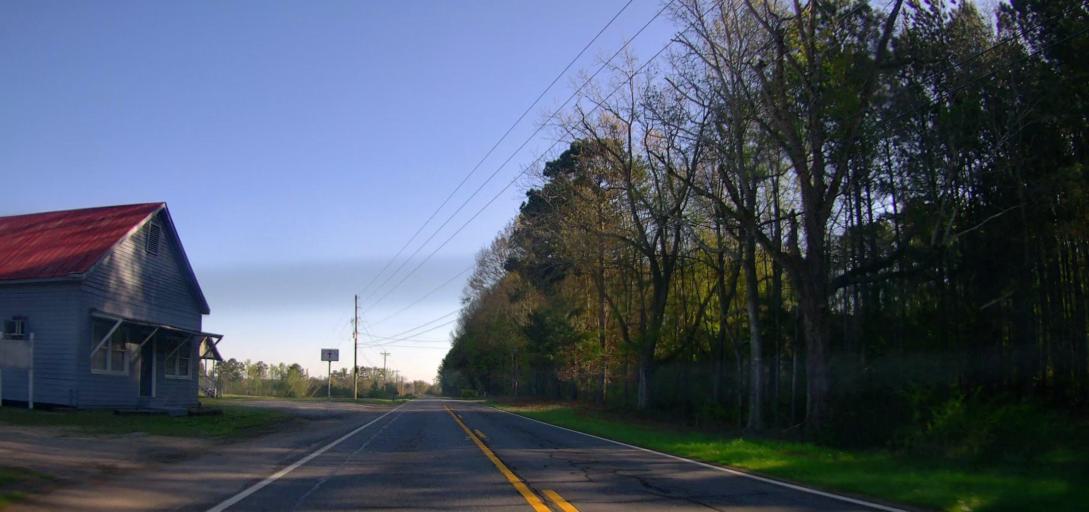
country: US
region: Georgia
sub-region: Butts County
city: Indian Springs
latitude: 33.1768
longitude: -83.9590
